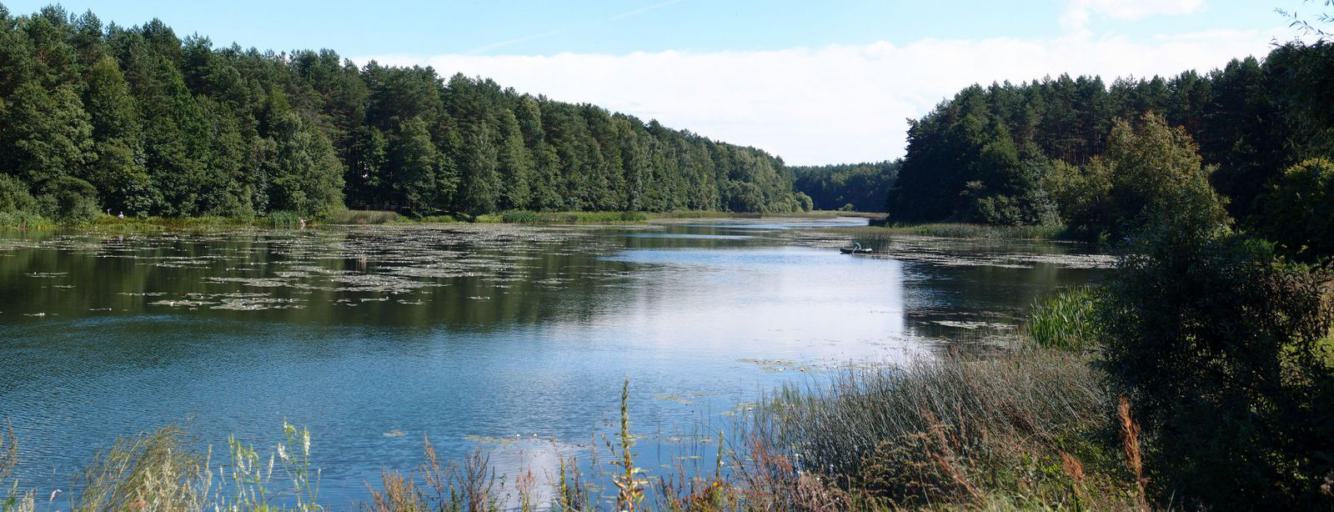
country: BY
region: Minsk
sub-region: Minski Rayon
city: Krasnaye
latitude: 54.1365
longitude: 26.9574
